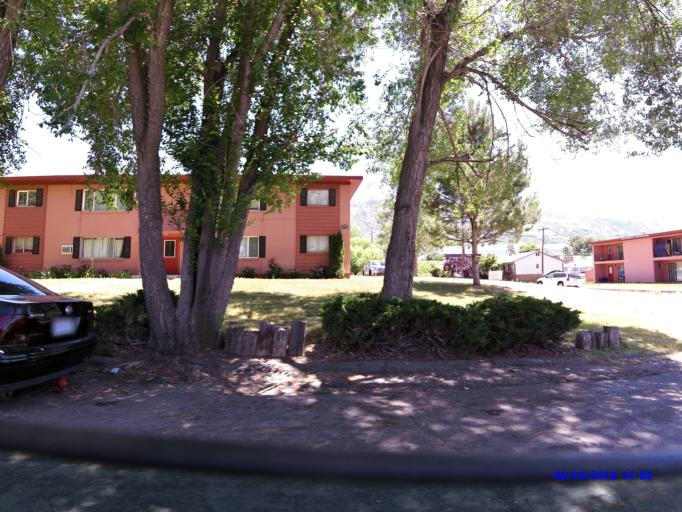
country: US
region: Utah
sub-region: Weber County
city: South Ogden
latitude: 41.2081
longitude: -111.9527
